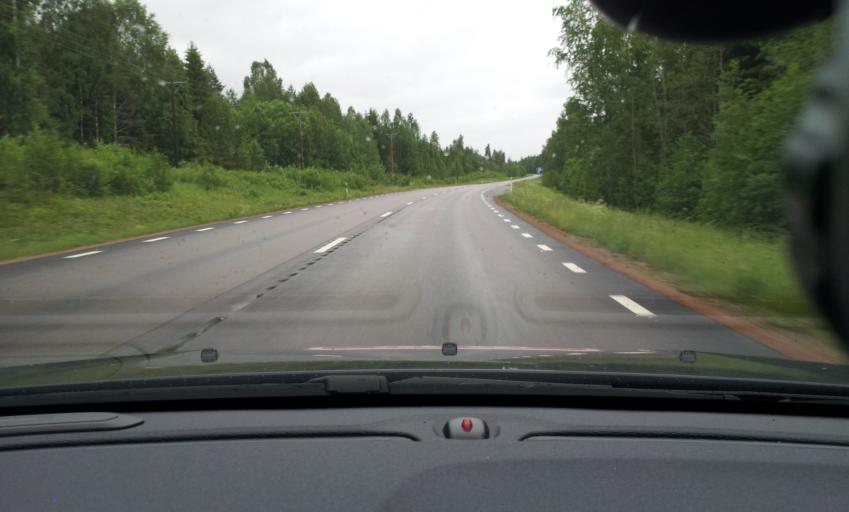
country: SE
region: Jaemtland
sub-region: Ragunda Kommun
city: Hammarstrand
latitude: 63.1722
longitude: 15.9532
